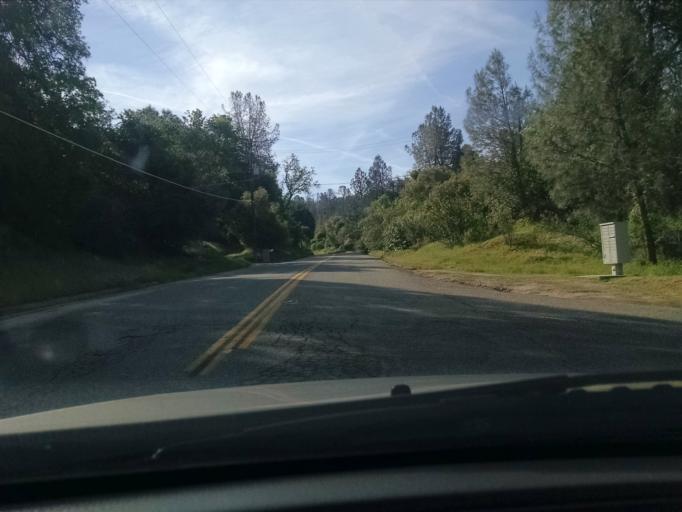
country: US
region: California
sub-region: Madera County
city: Oakhurst
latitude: 37.2933
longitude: -119.6457
